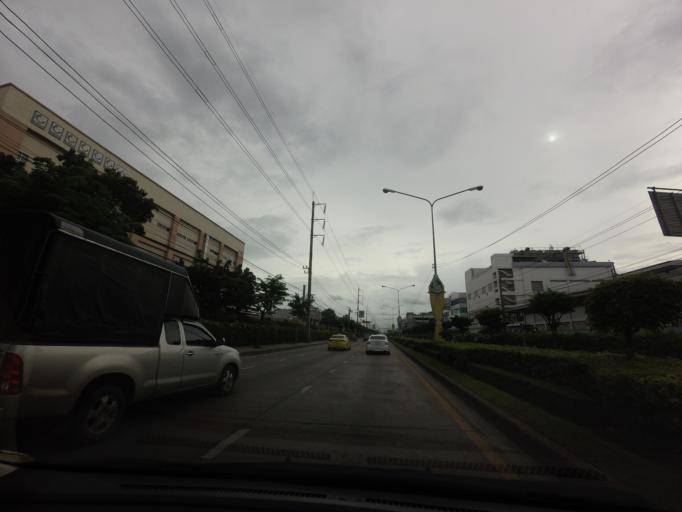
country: TH
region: Bangkok
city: Min Buri
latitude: 13.8024
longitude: 100.7079
